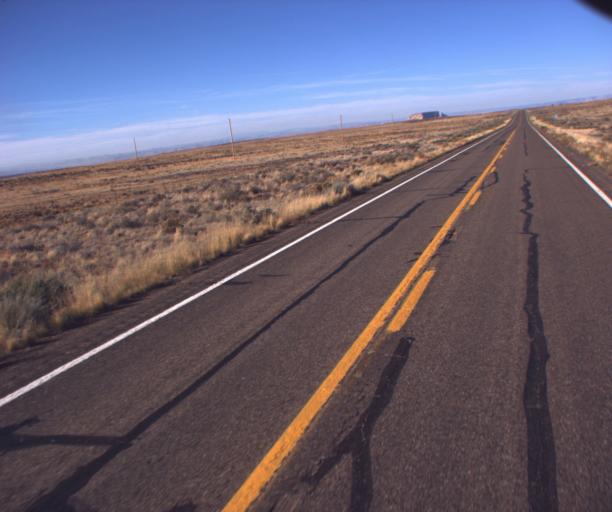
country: US
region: Arizona
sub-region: Coconino County
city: LeChee
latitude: 36.7452
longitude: -111.2847
